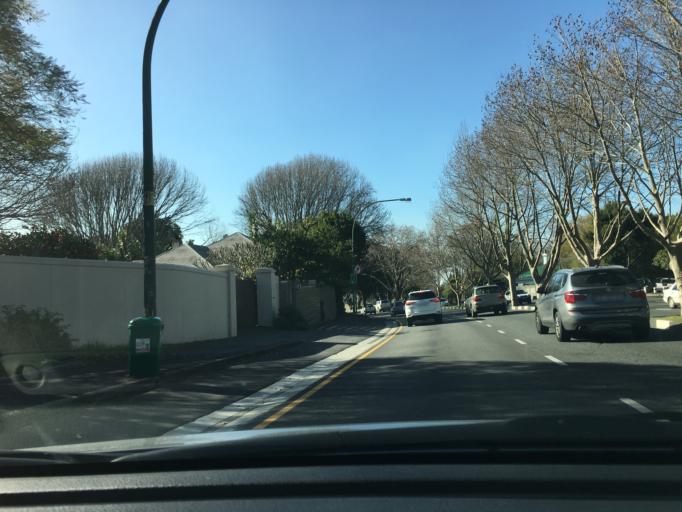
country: ZA
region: Western Cape
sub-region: City of Cape Town
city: Newlands
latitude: -33.9854
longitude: 18.4519
